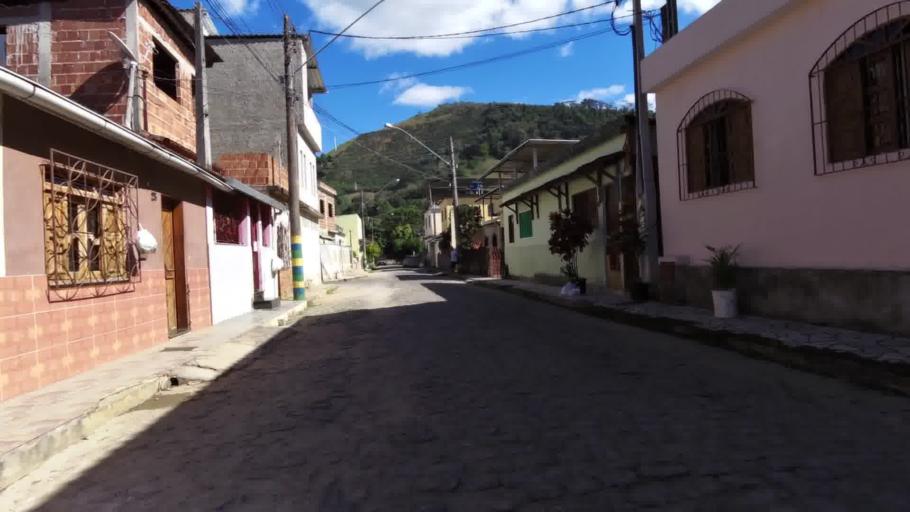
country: BR
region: Espirito Santo
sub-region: Rio Novo Do Sul
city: Rio Novo do Sul
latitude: -20.8626
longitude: -40.9315
